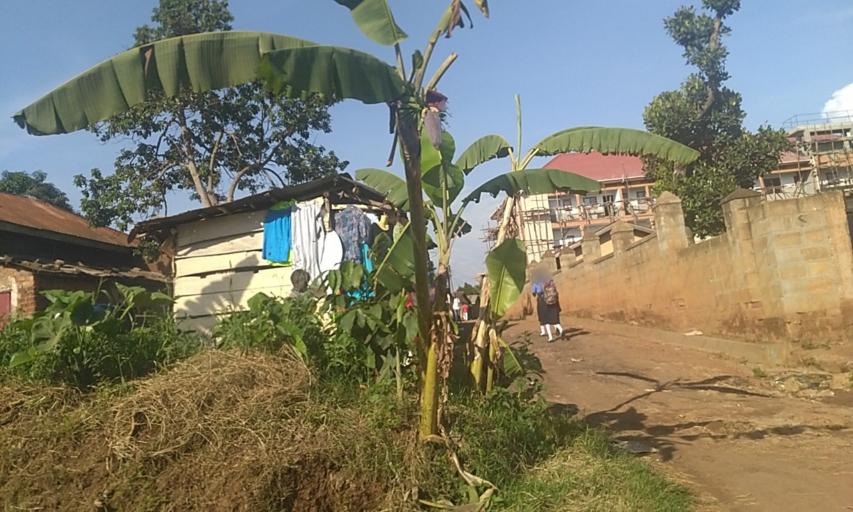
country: UG
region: Central Region
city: Kampala Central Division
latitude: 0.3171
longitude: 32.5518
